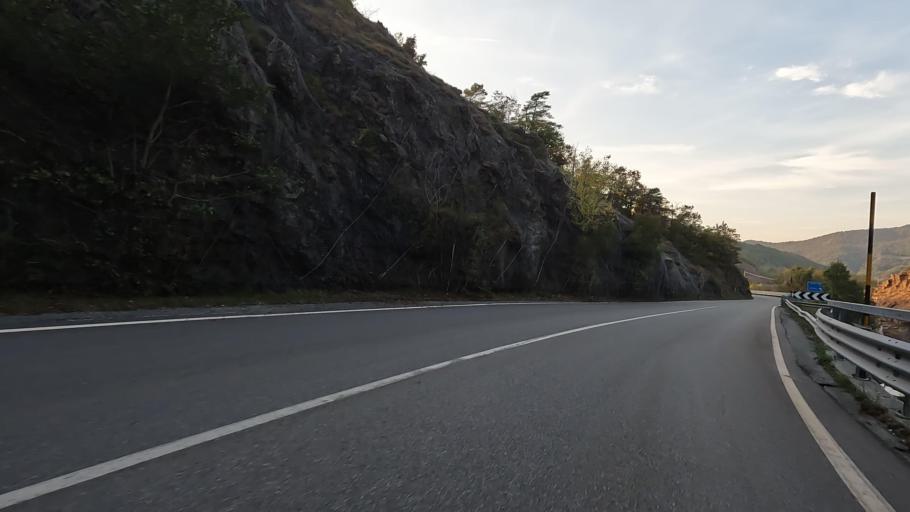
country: IT
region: Liguria
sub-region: Provincia di Savona
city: Sassello
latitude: 44.5197
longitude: 8.4717
